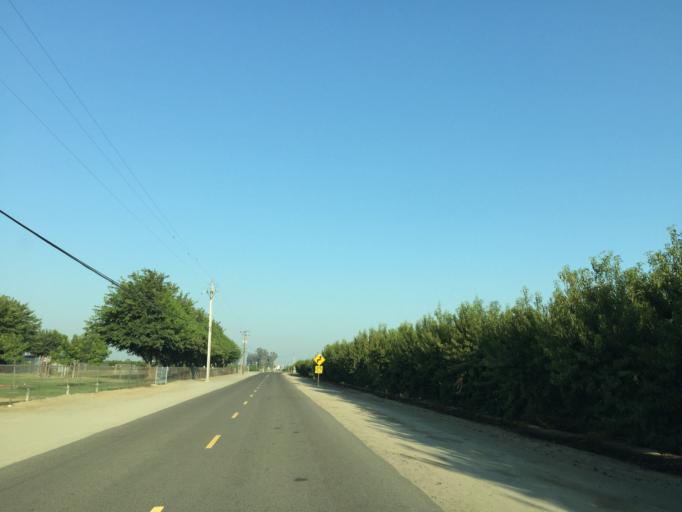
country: US
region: California
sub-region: Tulare County
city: London
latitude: 36.4590
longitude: -119.4807
